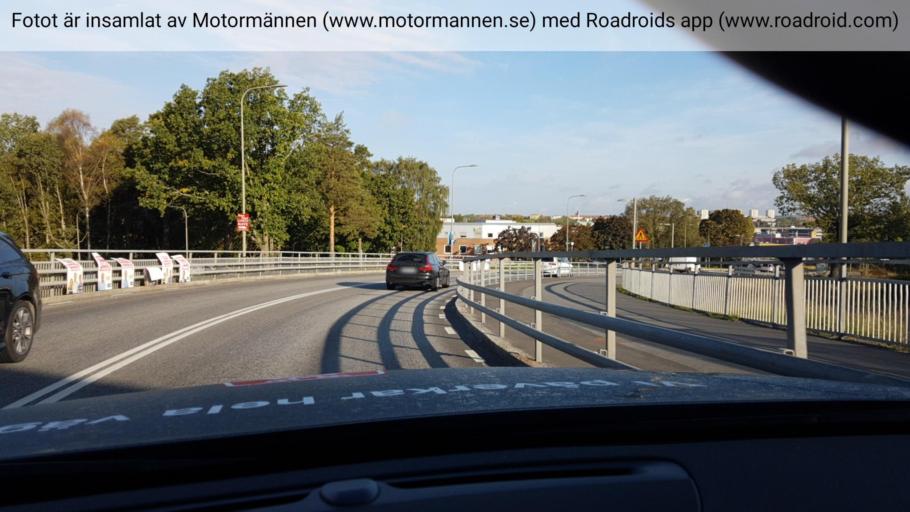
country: SE
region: Stockholm
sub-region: Stockholms Kommun
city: Arsta
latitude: 59.2884
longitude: 18.0190
